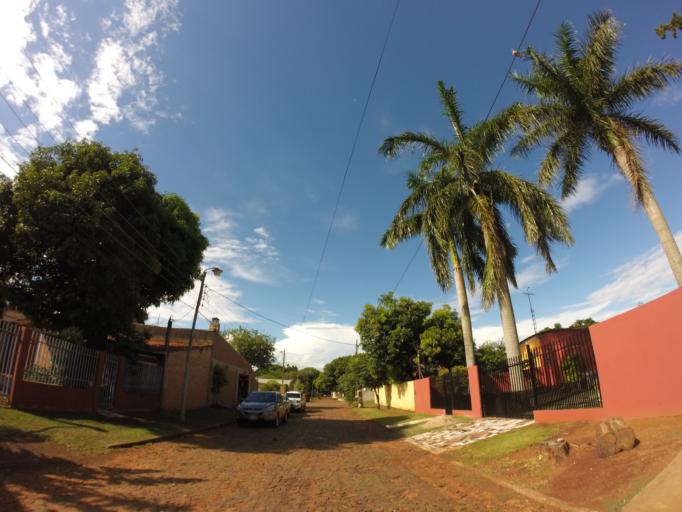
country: PY
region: Alto Parana
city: Ciudad del Este
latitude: -25.4046
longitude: -54.6263
